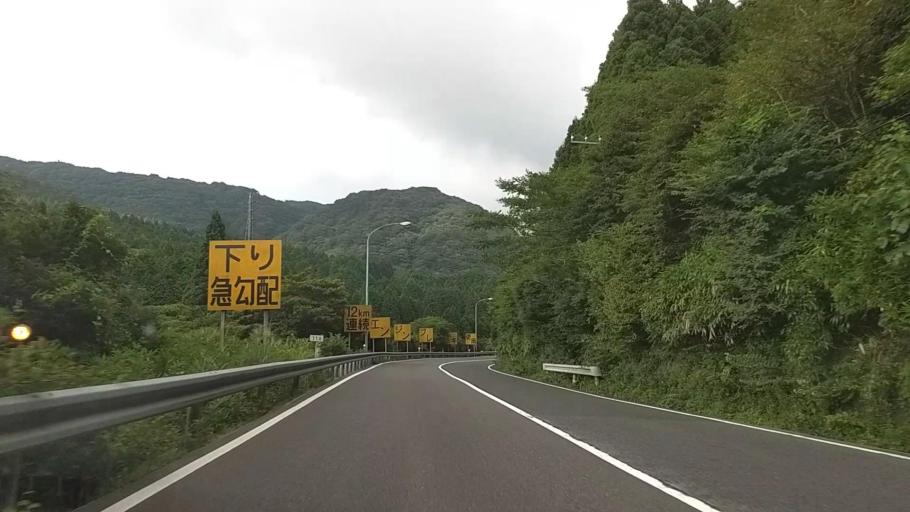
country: JP
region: Kanagawa
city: Hakone
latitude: 35.1864
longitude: 139.0338
